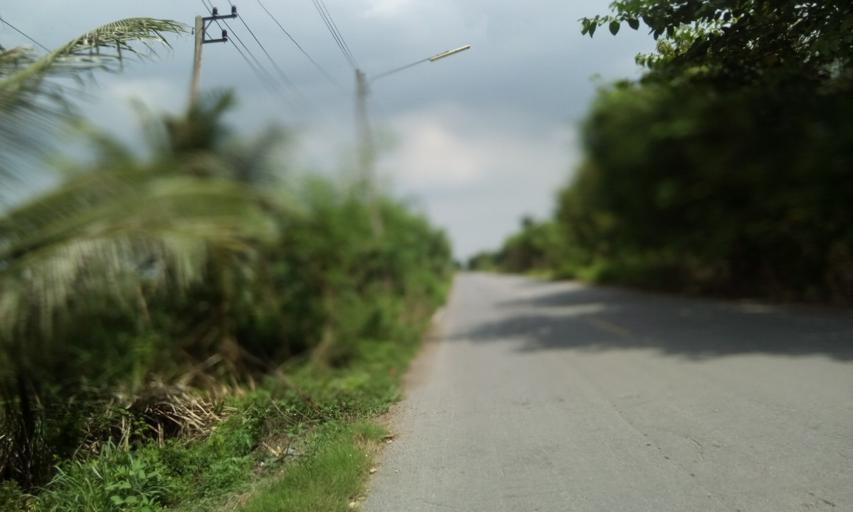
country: TH
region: Pathum Thani
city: Ban Rangsit
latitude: 14.0379
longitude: 100.8476
